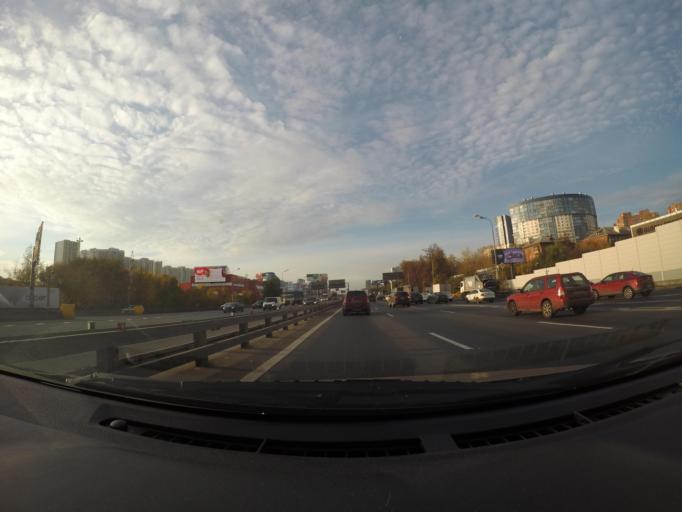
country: RU
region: Moscow
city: Khimki
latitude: 55.8832
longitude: 37.4431
